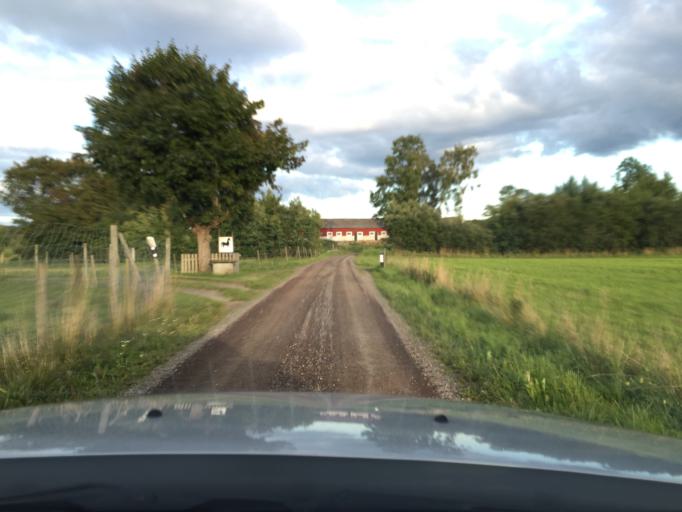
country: SE
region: Skane
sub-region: Hassleholms Kommun
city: Sosdala
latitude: 56.0291
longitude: 13.7281
